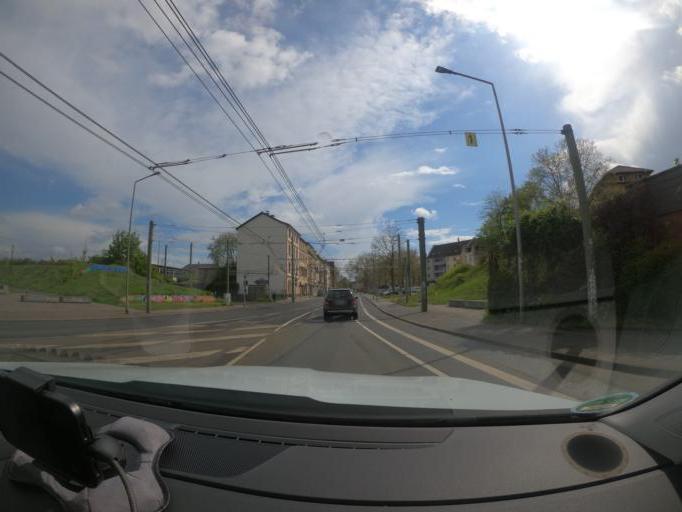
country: DE
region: North Rhine-Westphalia
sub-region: Regierungsbezirk Dusseldorf
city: Hochfeld
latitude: 51.4260
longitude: 6.7552
